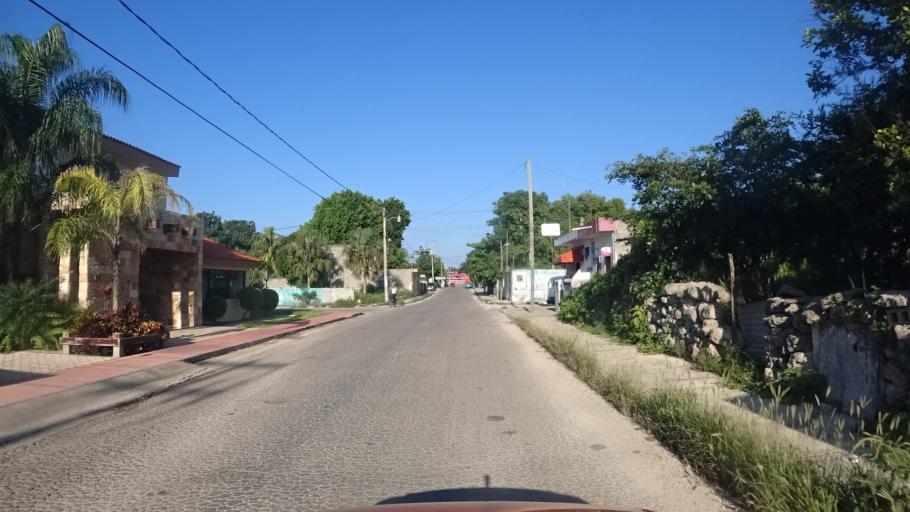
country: MX
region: Yucatan
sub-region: Tizimin
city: Tizimin
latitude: 21.1544
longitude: -88.1593
